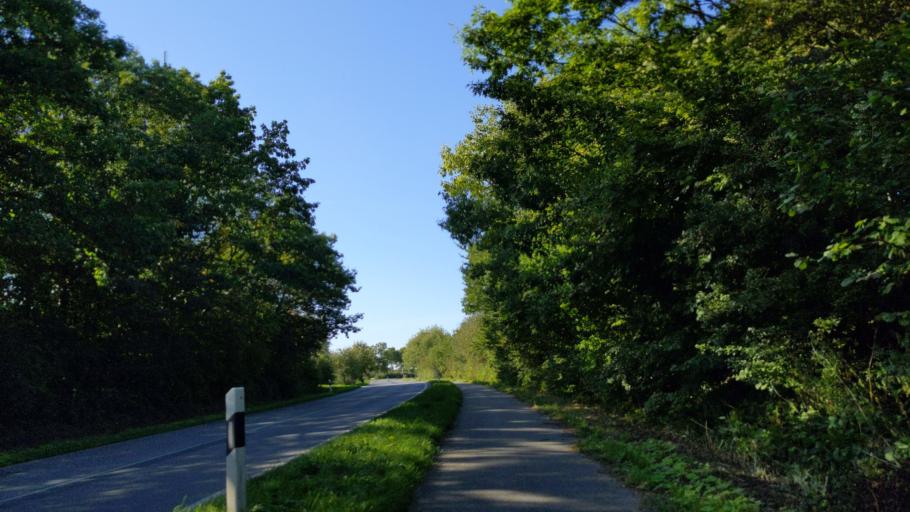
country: DE
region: Schleswig-Holstein
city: Ahrensbok
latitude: 53.9575
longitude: 10.6169
